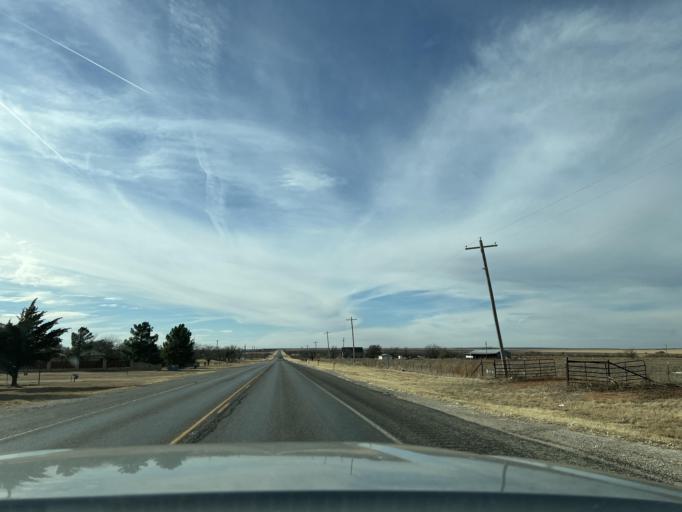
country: US
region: Texas
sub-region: Jones County
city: Anson
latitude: 32.7519
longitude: -99.9196
